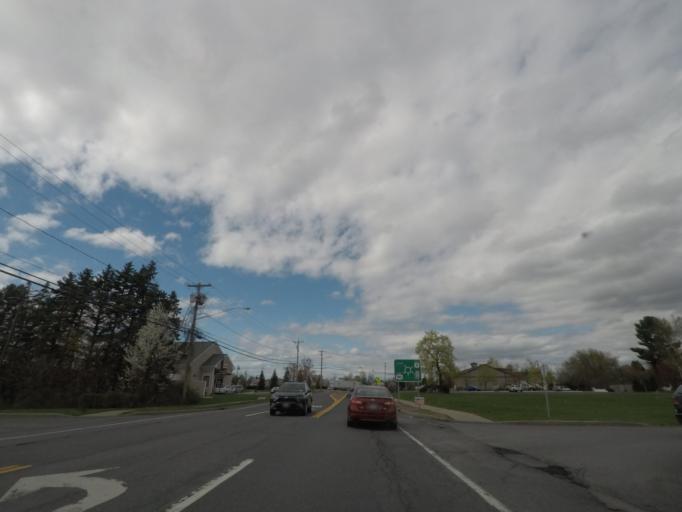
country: US
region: New York
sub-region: Columbia County
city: Valatie
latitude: 42.4269
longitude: -73.6879
